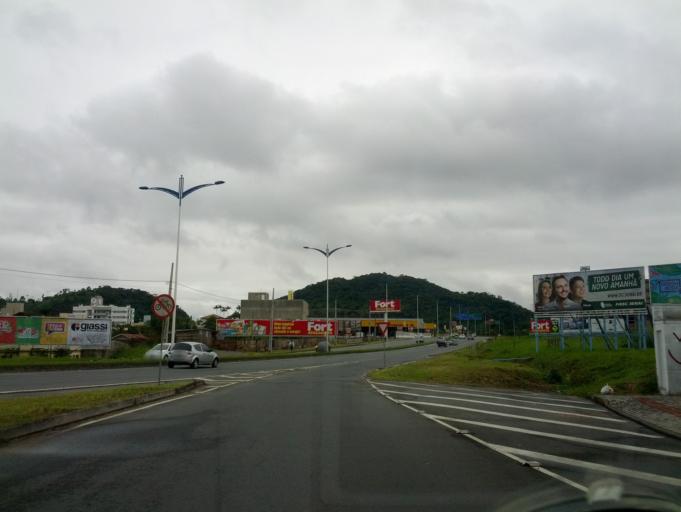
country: BR
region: Santa Catarina
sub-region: Blumenau
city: Blumenau
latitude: -26.8897
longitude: -49.0706
